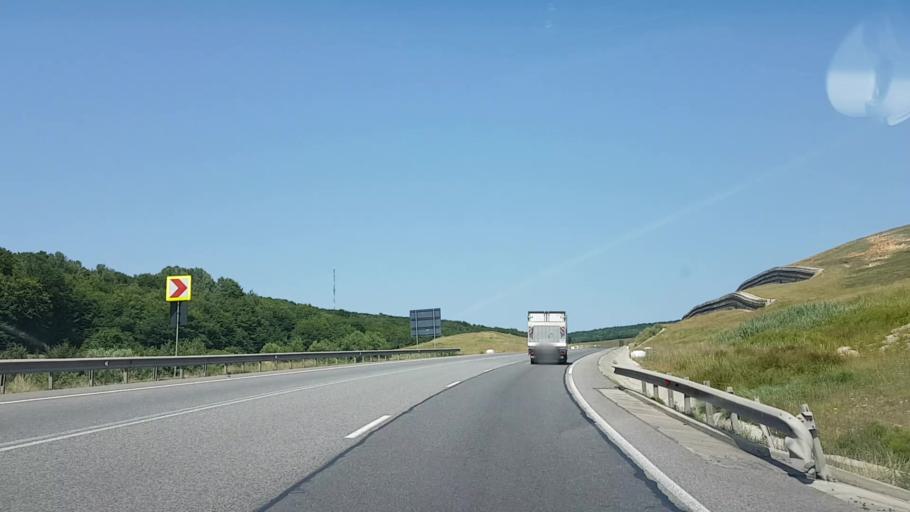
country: RO
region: Cluj
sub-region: Comuna Feleacu
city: Feleacu
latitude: 46.6960
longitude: 23.6361
